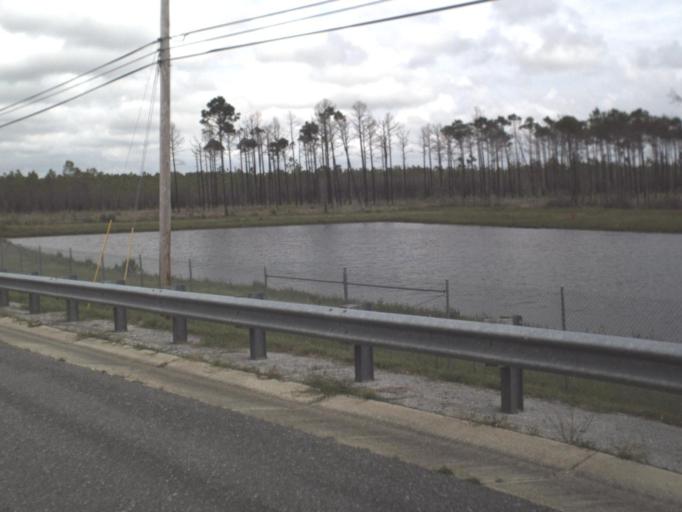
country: US
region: Florida
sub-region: Santa Rosa County
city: Bagdad
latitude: 30.5152
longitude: -87.0871
